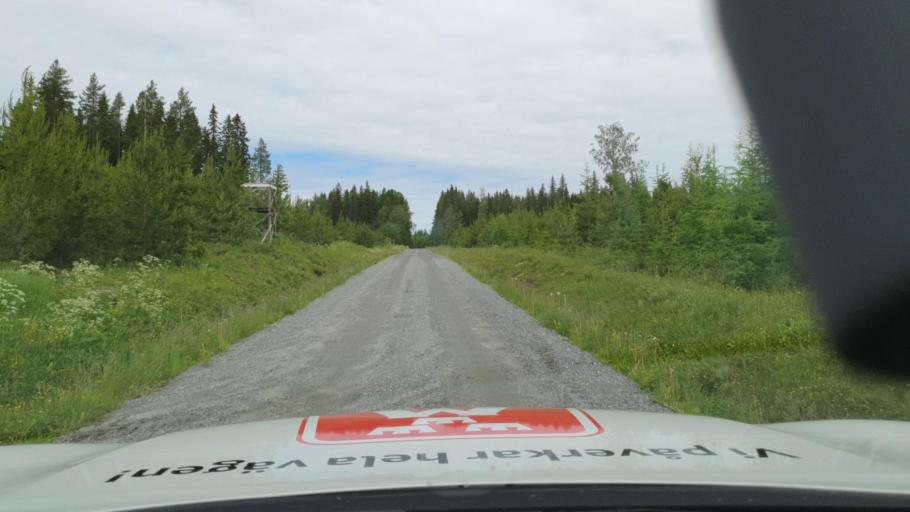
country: SE
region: Vaesterbotten
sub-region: Skelleftea Kommun
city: Langsele
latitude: 64.4725
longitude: 20.2649
